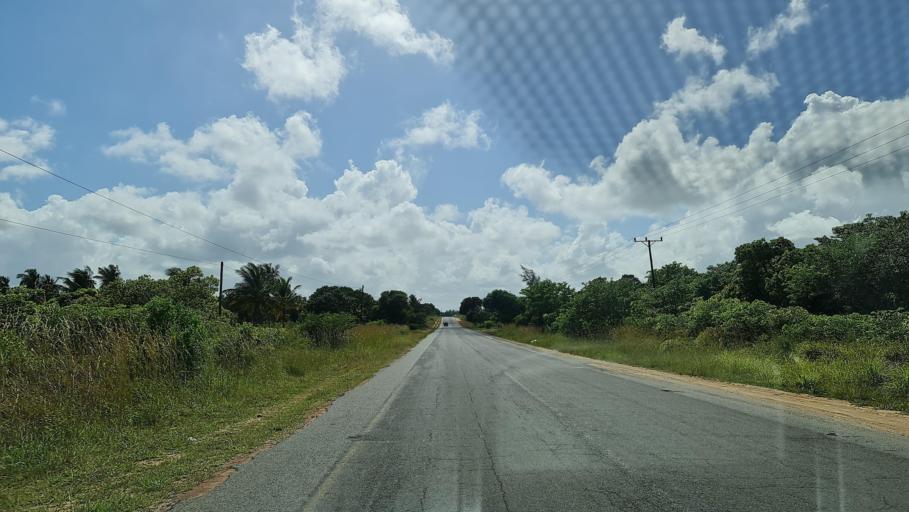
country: MZ
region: Gaza
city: Manjacaze
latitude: -24.6765
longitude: 34.5645
